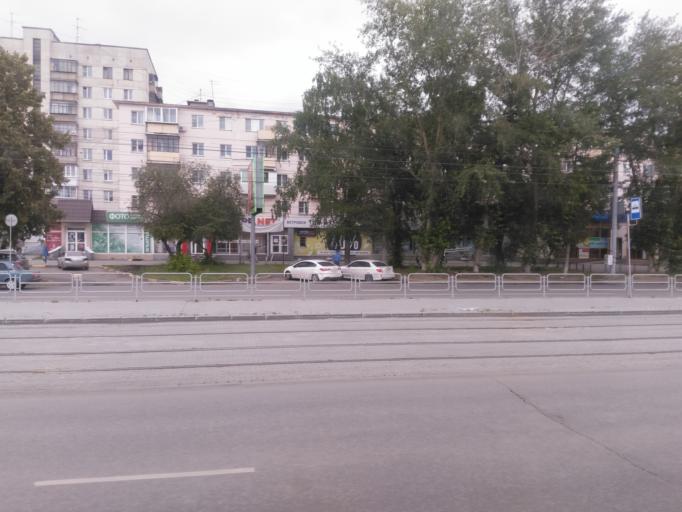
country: RU
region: Chelyabinsk
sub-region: Gorod Chelyabinsk
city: Chelyabinsk
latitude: 55.1836
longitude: 61.3987
